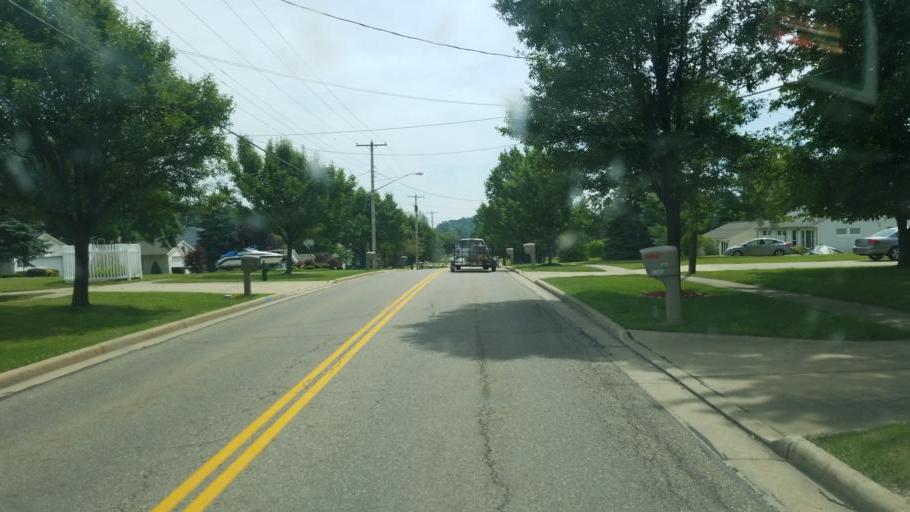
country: US
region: Ohio
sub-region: Summit County
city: Twinsburg
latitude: 41.3403
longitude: -81.4678
